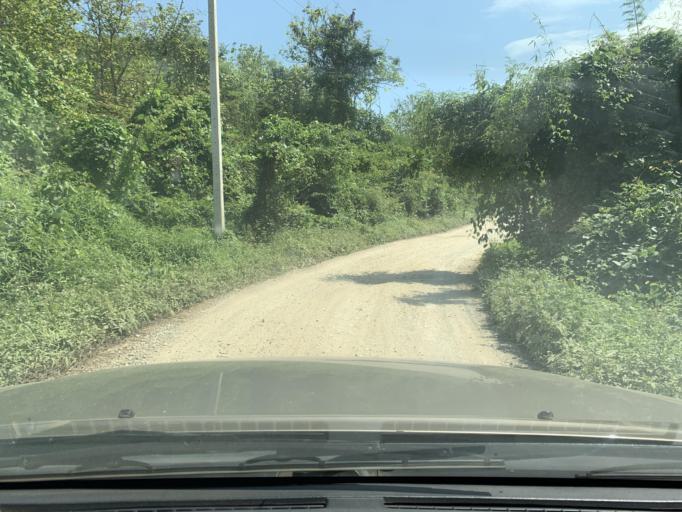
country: LA
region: Louangphabang
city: Louangphabang
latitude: 19.8929
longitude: 102.2026
